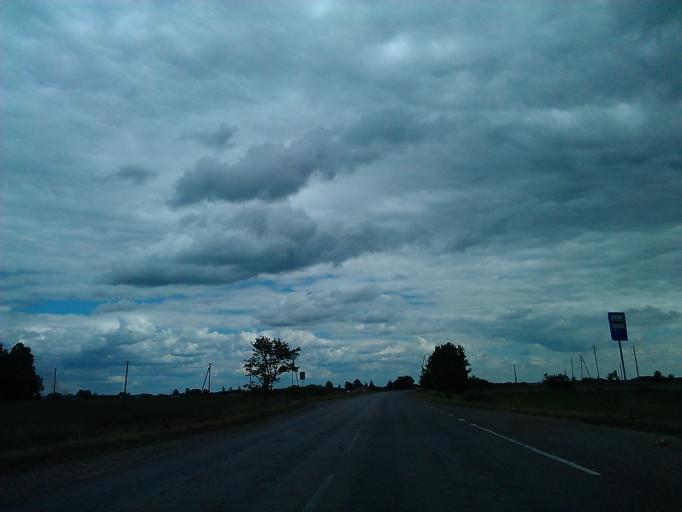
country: LV
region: Dobeles Rajons
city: Dobele
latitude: 56.6304
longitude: 23.3182
